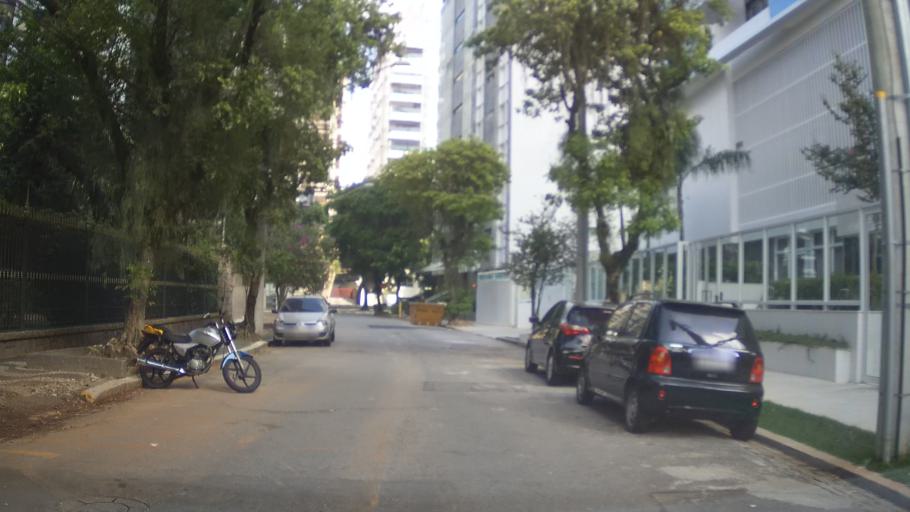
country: BR
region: Sao Paulo
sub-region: Santos
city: Santos
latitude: -23.9671
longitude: -46.3278
